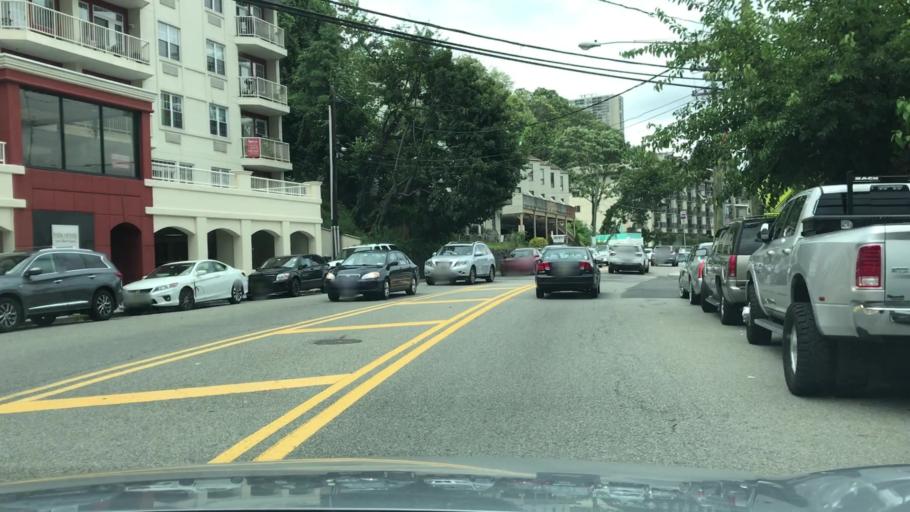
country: US
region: New Jersey
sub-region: Bergen County
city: Edgewater
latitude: 40.8319
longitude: -73.9725
